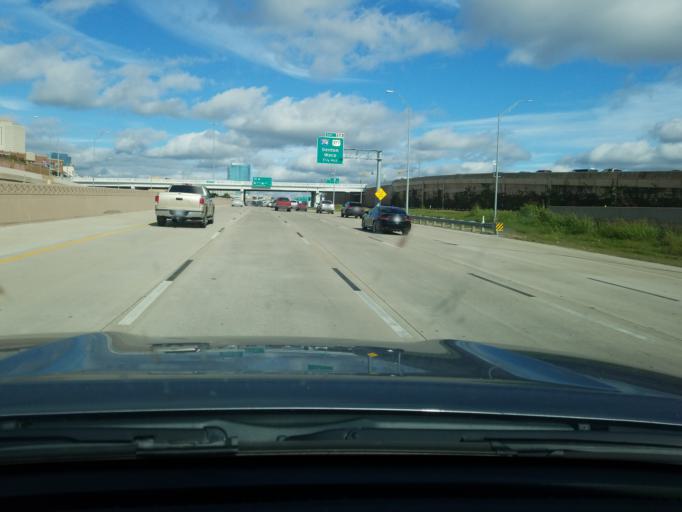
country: US
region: Texas
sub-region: Tarrant County
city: Fort Worth
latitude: 32.7413
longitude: -97.3439
